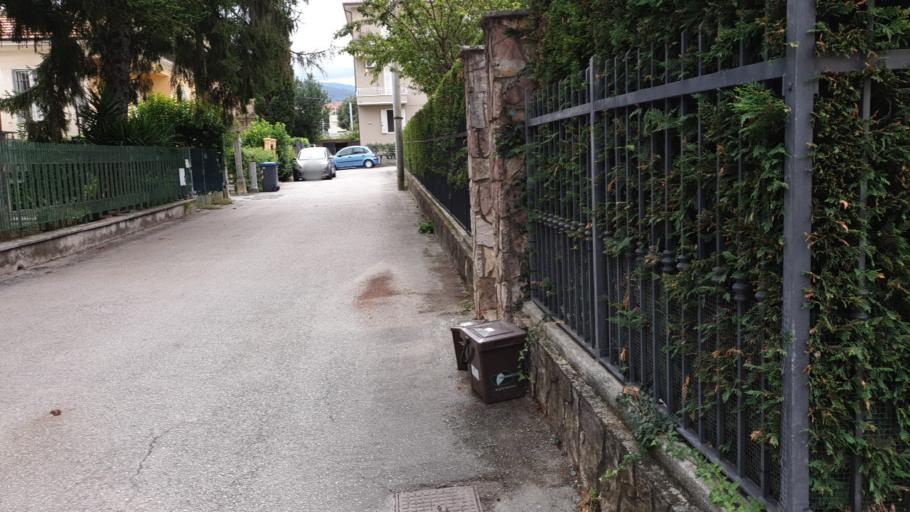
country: IT
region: Umbria
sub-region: Provincia di Perugia
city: Foligno
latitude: 42.9605
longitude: 12.7107
